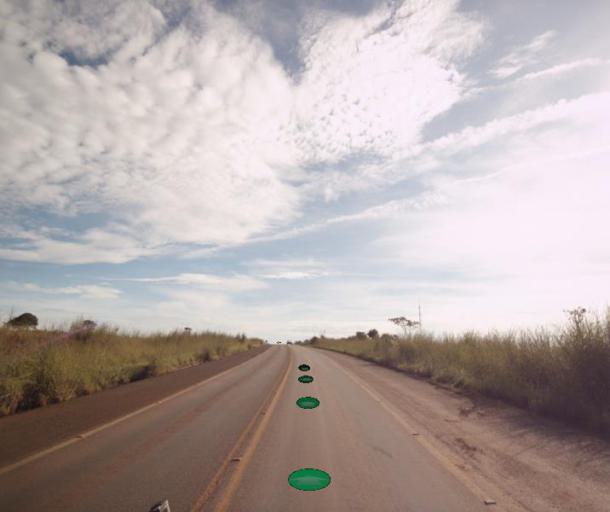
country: BR
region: Federal District
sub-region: Brasilia
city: Brasilia
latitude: -15.7500
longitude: -48.4121
